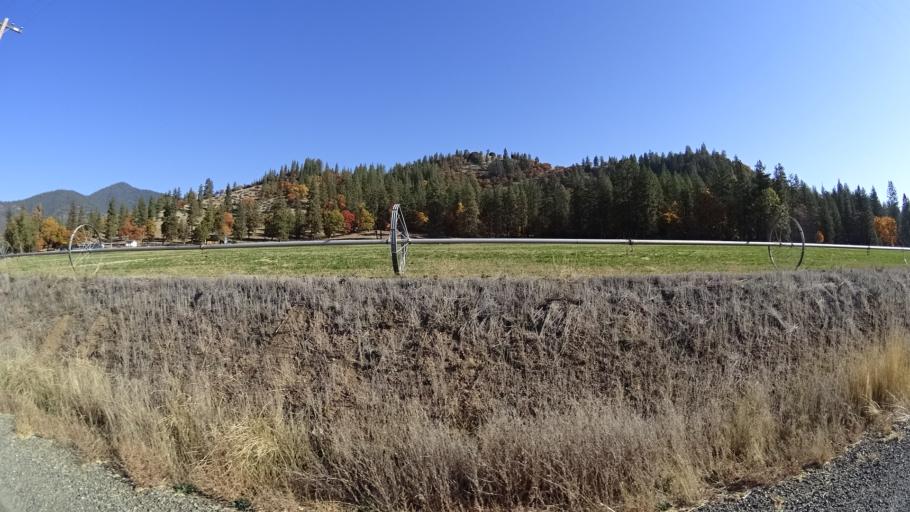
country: US
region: California
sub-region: Siskiyou County
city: Yreka
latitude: 41.6375
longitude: -122.9085
